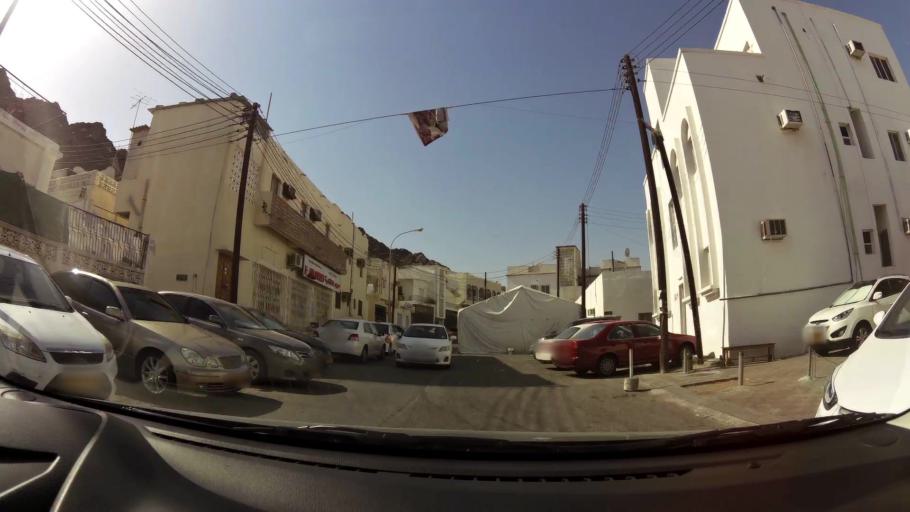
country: OM
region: Muhafazat Masqat
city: Muscat
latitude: 23.6072
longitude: 58.5534
